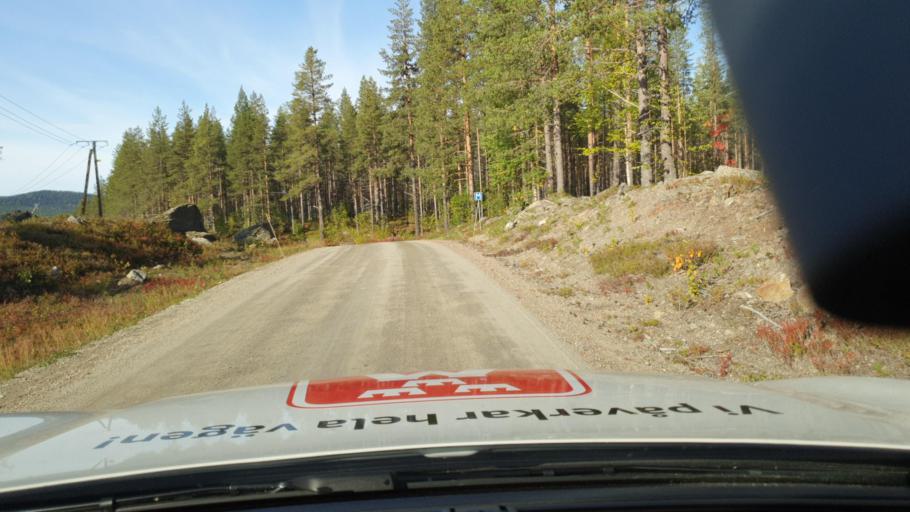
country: SE
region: Vaesterbotten
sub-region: Asele Kommun
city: Asele
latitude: 63.9889
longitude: 17.8332
